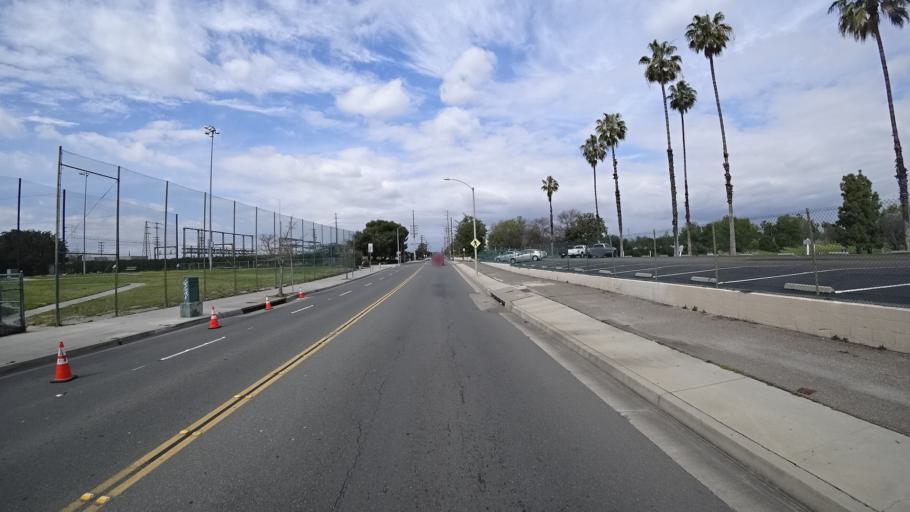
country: US
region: California
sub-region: Orange County
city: Stanton
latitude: 33.8364
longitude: -117.9677
